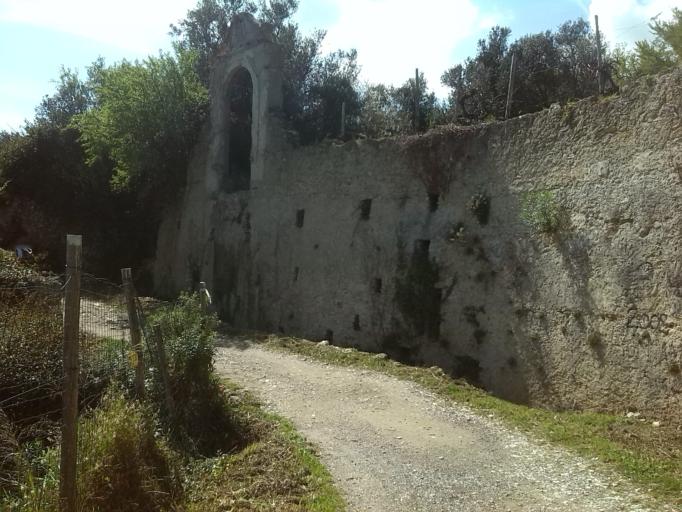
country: IT
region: Liguria
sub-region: Provincia di Savona
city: Albenga
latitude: 44.0417
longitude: 8.2071
